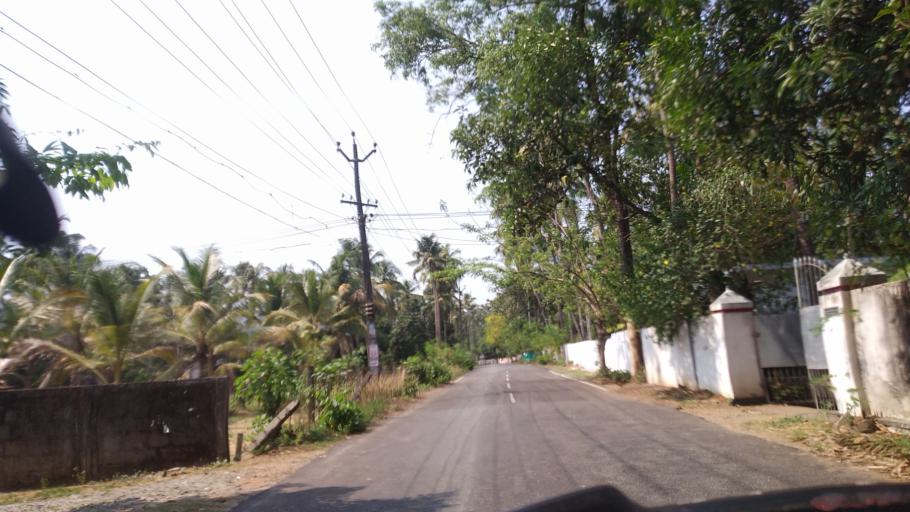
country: IN
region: Kerala
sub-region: Thrissur District
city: Thanniyam
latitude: 10.3662
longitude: 76.1066
